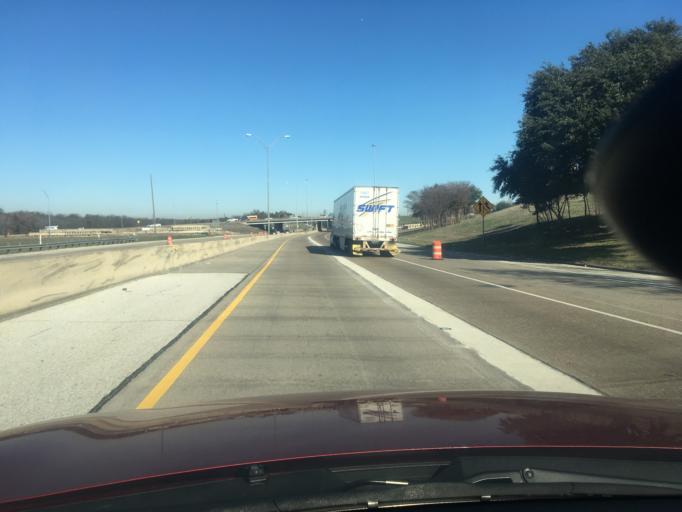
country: US
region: Texas
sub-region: Dallas County
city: Cockrell Hill
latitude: 32.6887
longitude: -96.8473
